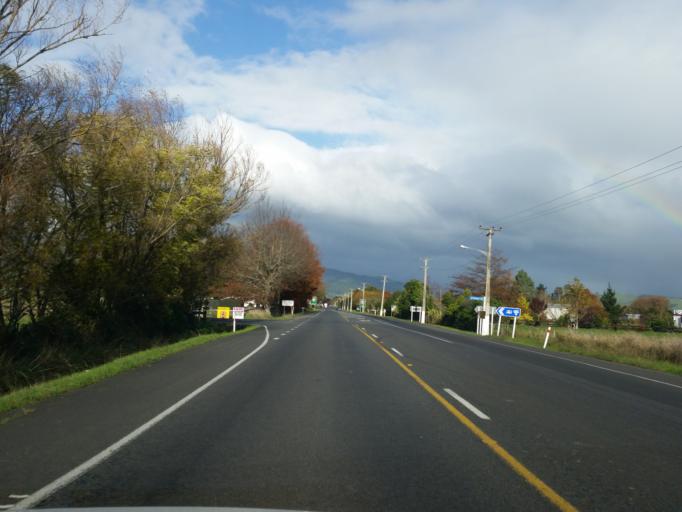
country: NZ
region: Waikato
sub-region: Hauraki District
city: Paeroa
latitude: -37.3658
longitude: 175.6587
